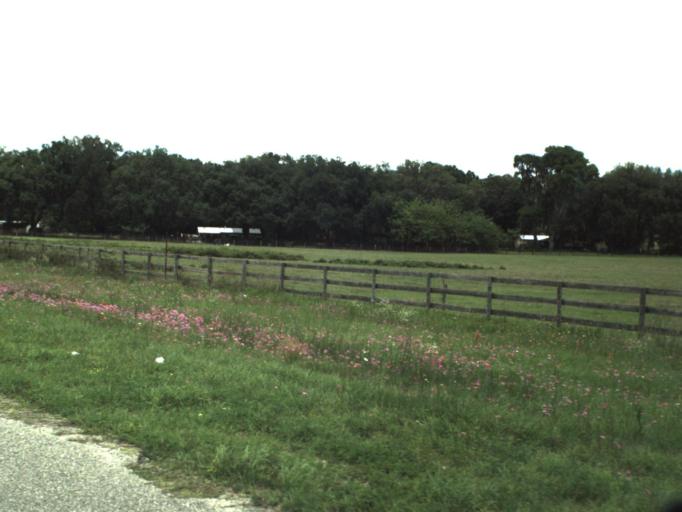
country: US
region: Florida
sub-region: Marion County
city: Citra
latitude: 29.3759
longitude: -82.1756
